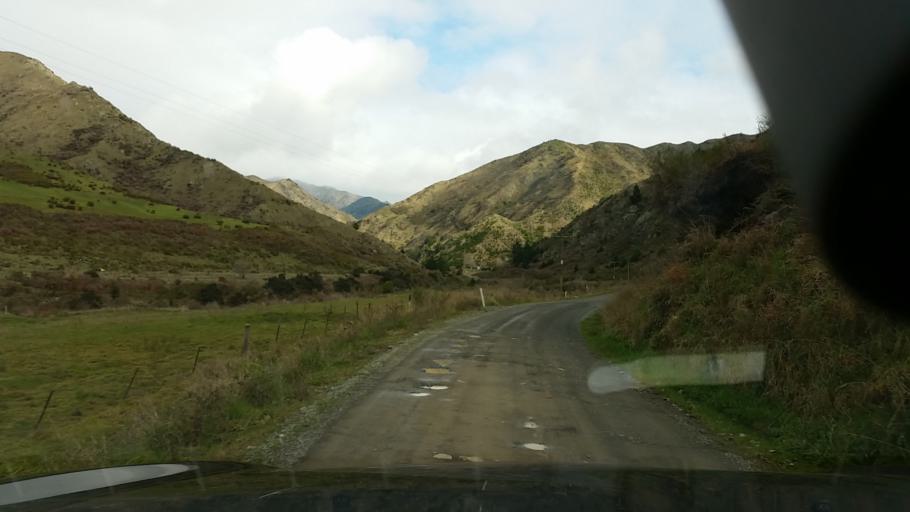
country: NZ
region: Tasman
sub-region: Tasman District
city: Richmond
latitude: -41.7120
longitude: 173.4826
